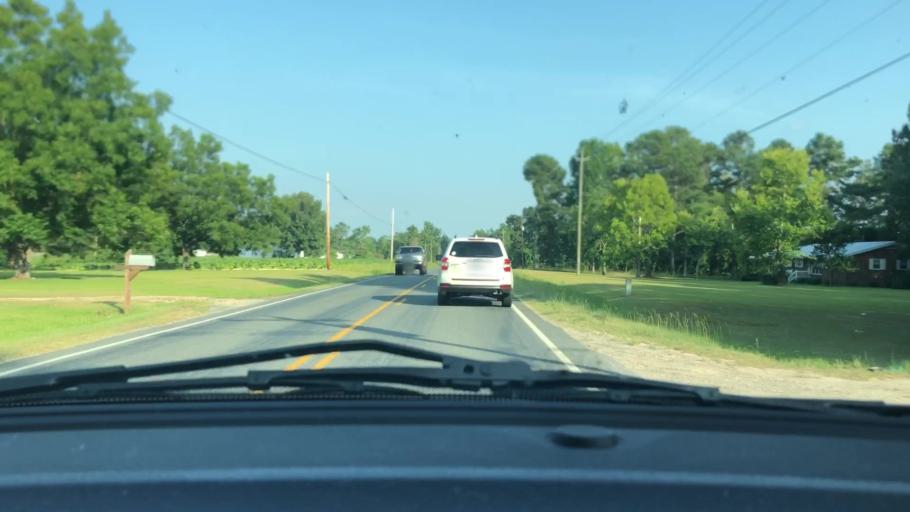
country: US
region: North Carolina
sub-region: Lee County
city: Broadway
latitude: 35.3515
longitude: -79.0736
